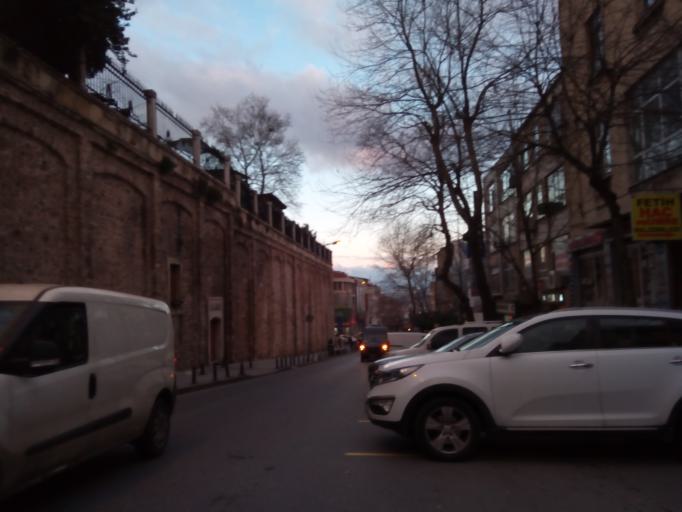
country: TR
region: Istanbul
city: Eminoenue
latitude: 41.0140
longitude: 28.9658
